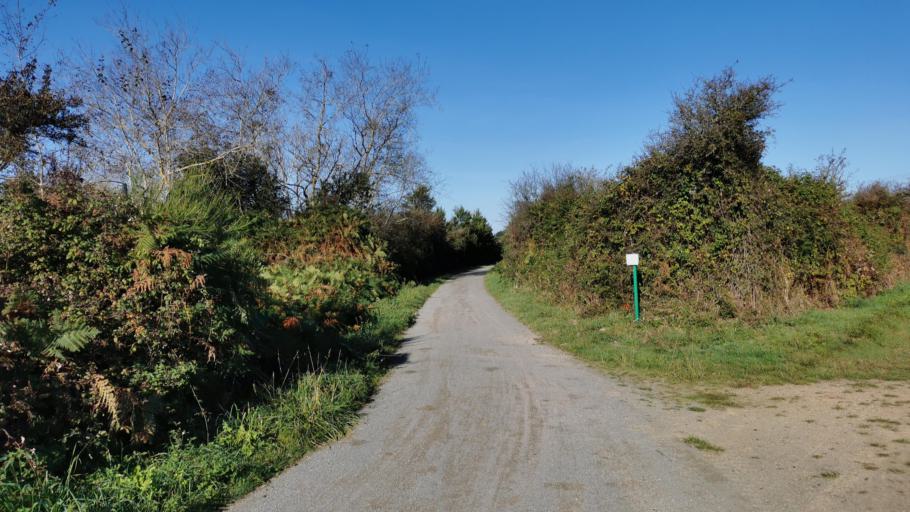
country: FR
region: Brittany
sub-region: Departement du Morbihan
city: Saint-Gildas-de-Rhuys
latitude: 47.5292
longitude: -2.8392
